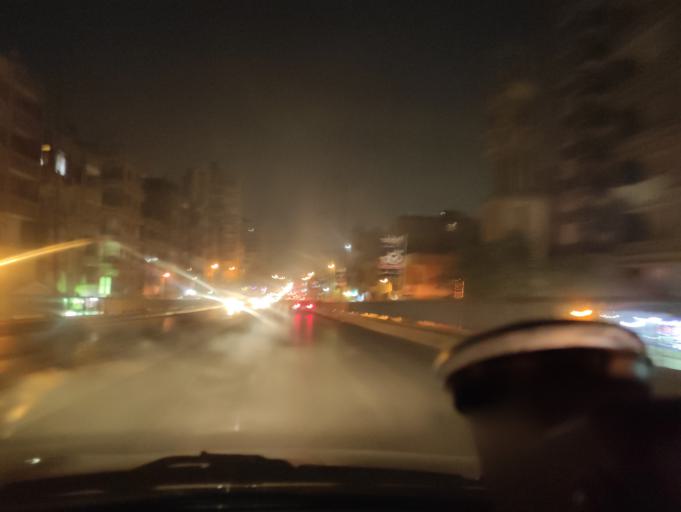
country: EG
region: Muhafazat al Qahirah
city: Cairo
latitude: 30.0922
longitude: 31.2783
